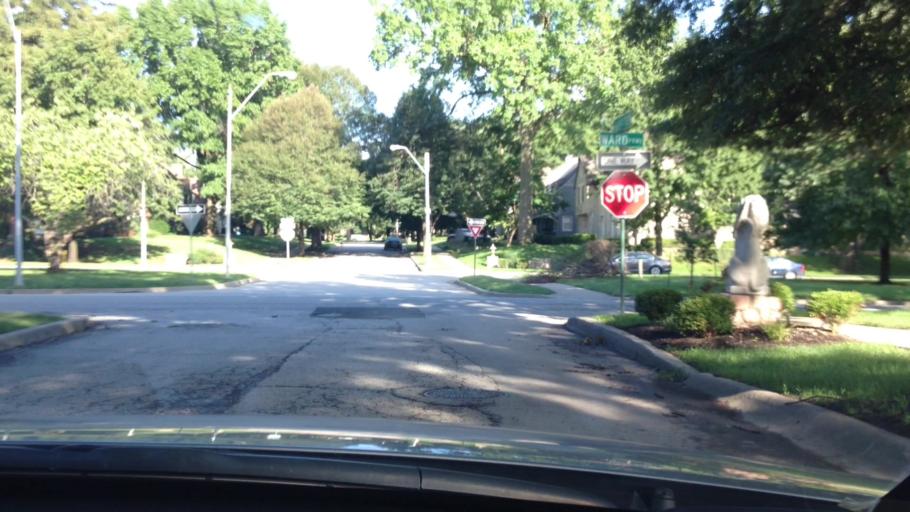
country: US
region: Kansas
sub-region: Johnson County
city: Mission Hills
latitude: 39.0033
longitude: -94.6036
